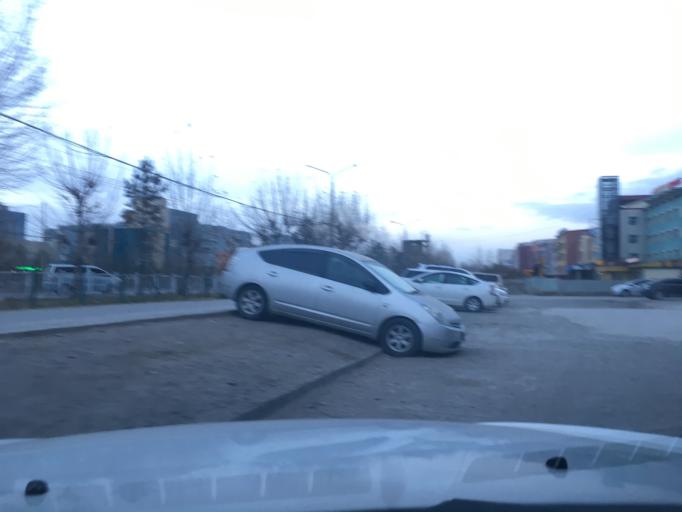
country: MN
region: Ulaanbaatar
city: Ulaanbaatar
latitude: 47.9132
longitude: 106.8640
